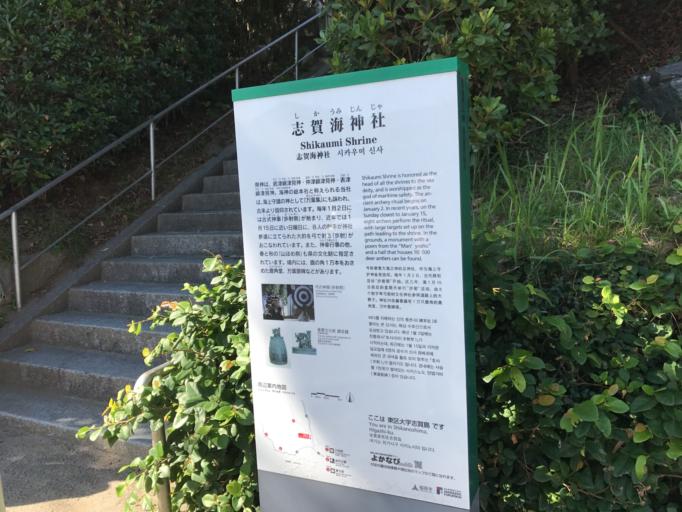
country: JP
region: Fukuoka
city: Fukuoka-shi
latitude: 33.6664
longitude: 130.3135
